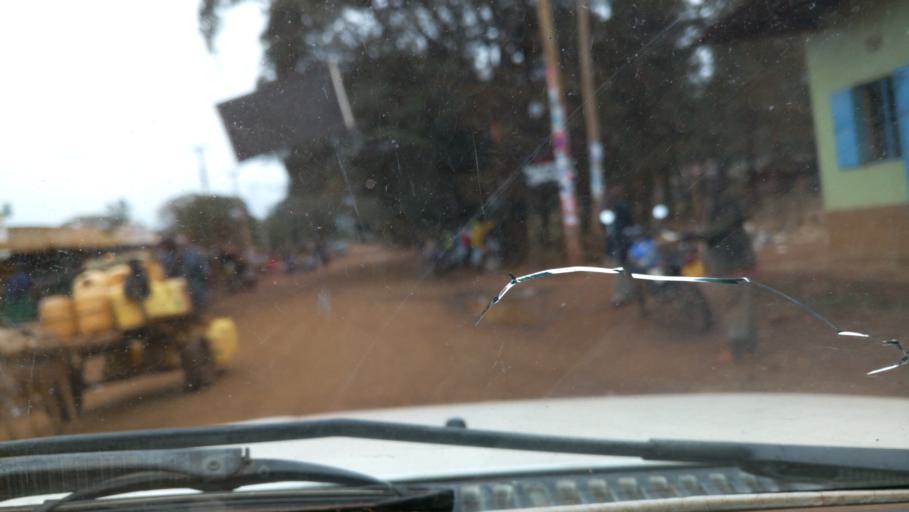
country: KE
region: Murang'a District
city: Maragua
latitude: -0.8447
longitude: 37.1792
